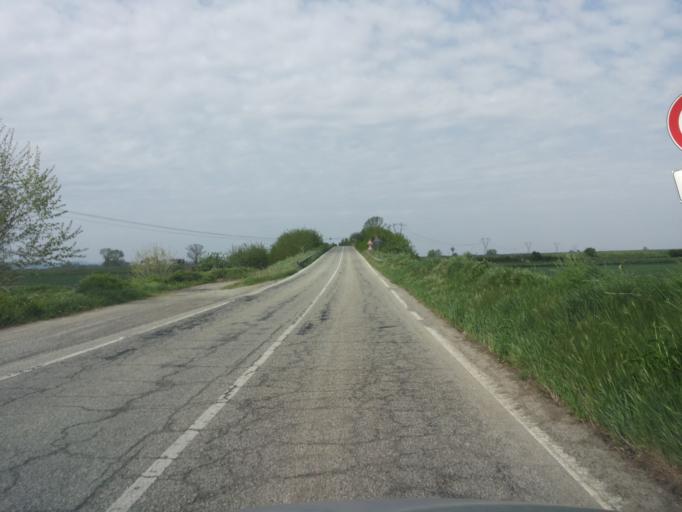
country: IT
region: Piedmont
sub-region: Provincia di Vercelli
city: Motta De Conti
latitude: 45.1853
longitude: 8.5007
